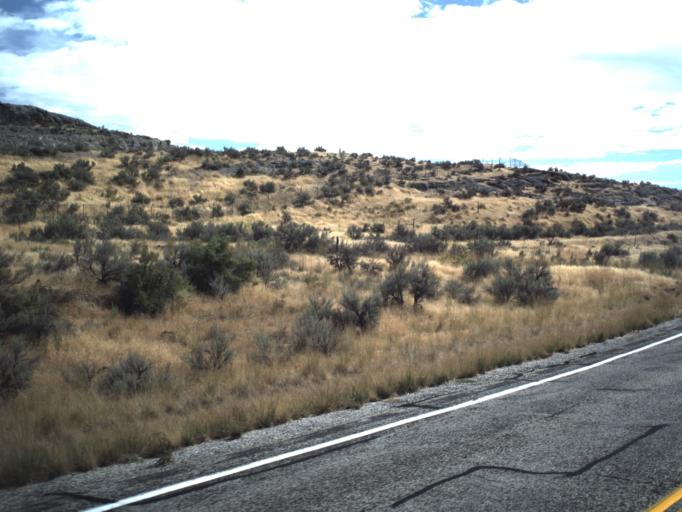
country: US
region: Utah
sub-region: Box Elder County
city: Tremonton
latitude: 41.6714
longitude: -112.4473
